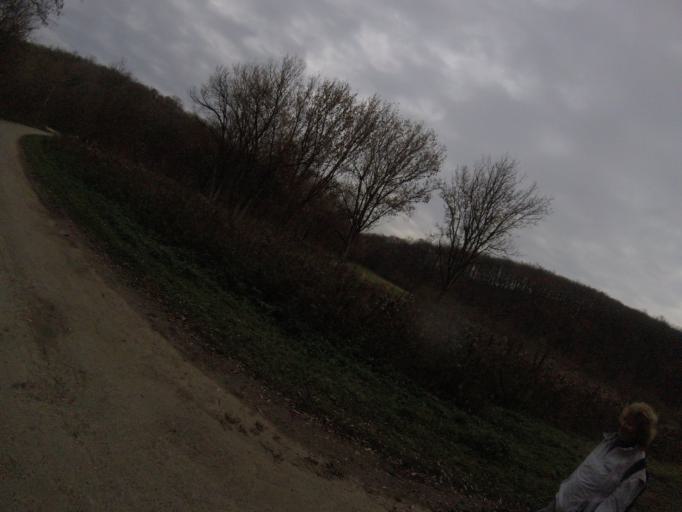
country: HU
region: Tolna
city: Szentgalpuszta
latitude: 46.3409
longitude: 18.6219
